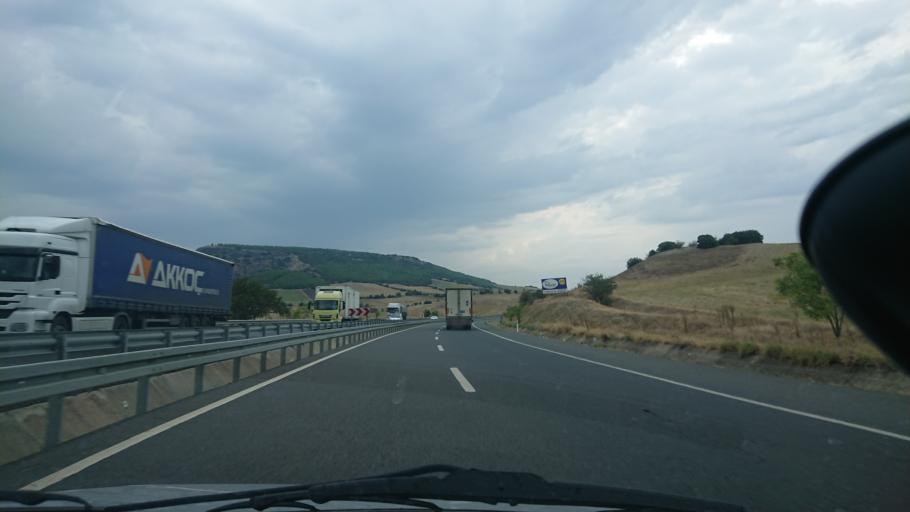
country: TR
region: Manisa
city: Selendi
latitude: 38.6163
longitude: 28.8776
